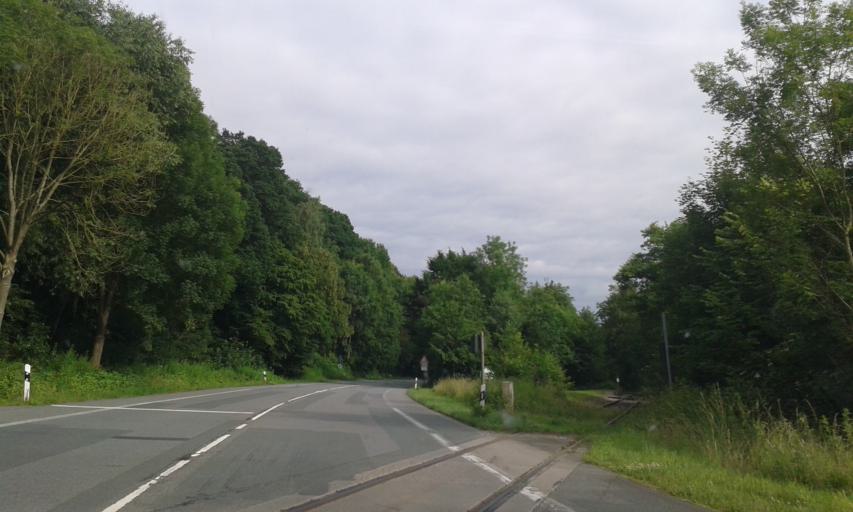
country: DE
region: Lower Saxony
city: Rinteln
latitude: 52.1351
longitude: 9.0871
